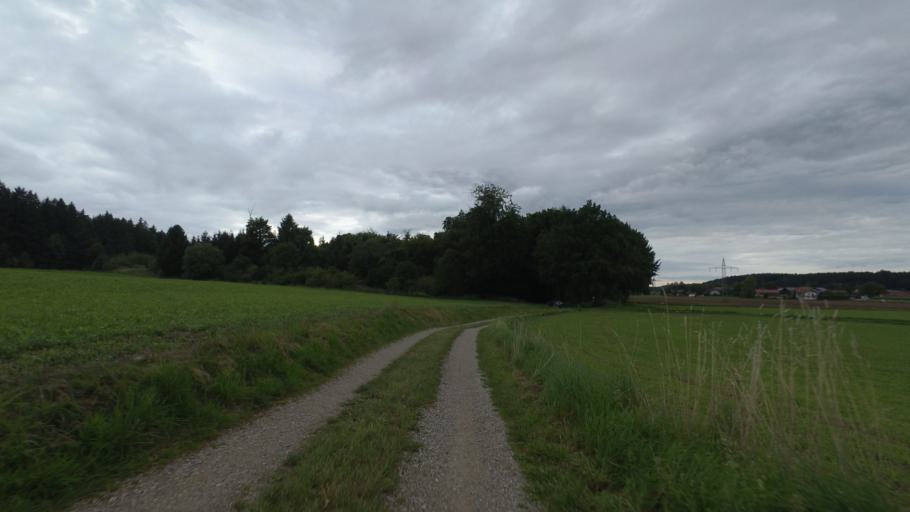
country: DE
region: Bavaria
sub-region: Upper Bavaria
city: Nussdorf
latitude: 47.8826
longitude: 12.5802
